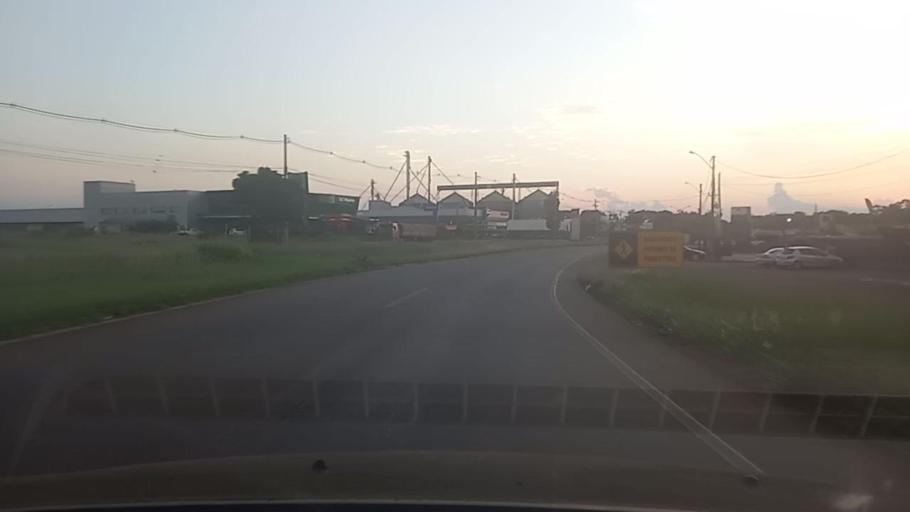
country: BR
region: Rio Grande do Sul
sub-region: Passo Fundo
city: Passo Fundo
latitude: -28.2720
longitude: -52.4421
